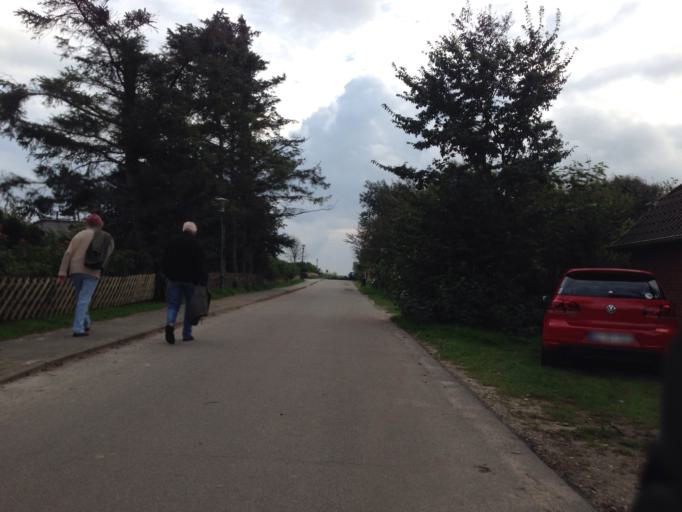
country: DE
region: Schleswig-Holstein
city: Borgsum
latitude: 54.6854
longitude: 8.4683
